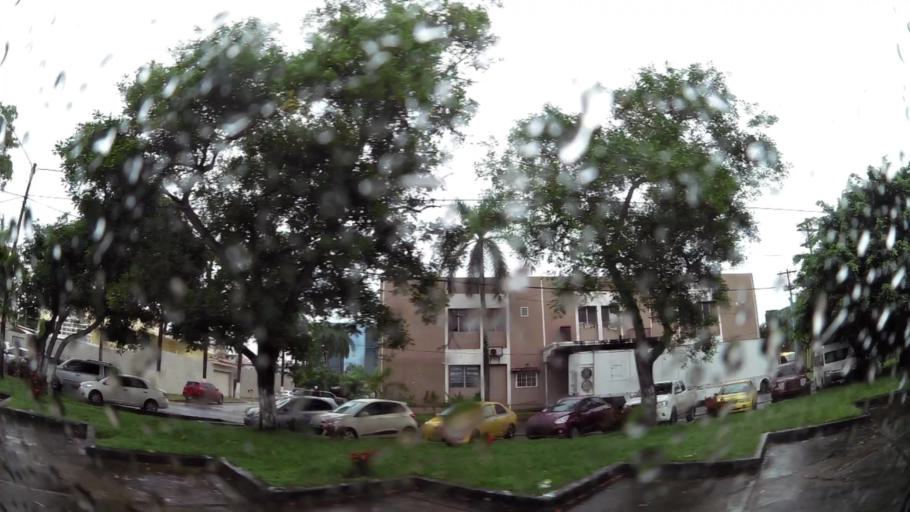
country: PA
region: Colon
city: Colon
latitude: 9.3567
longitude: -79.8952
